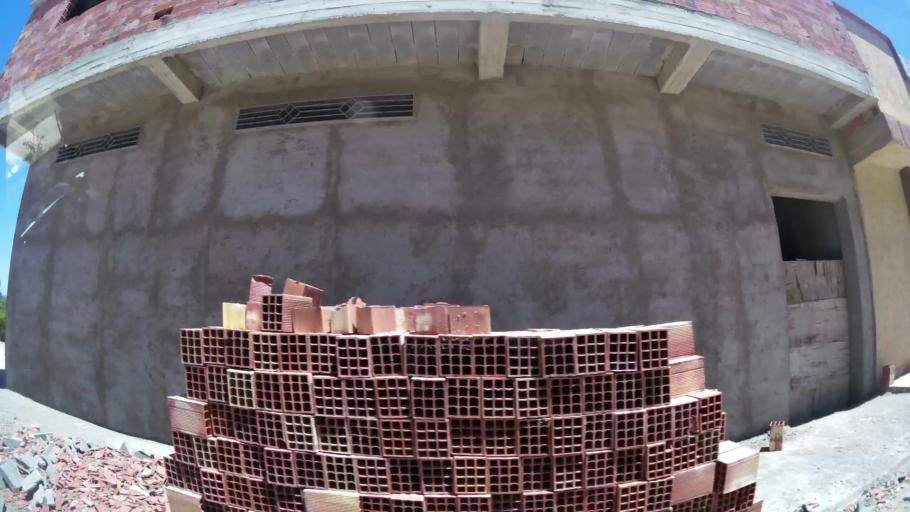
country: MA
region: Oriental
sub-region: Oujda-Angad
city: Oujda
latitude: 34.6779
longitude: -1.8543
